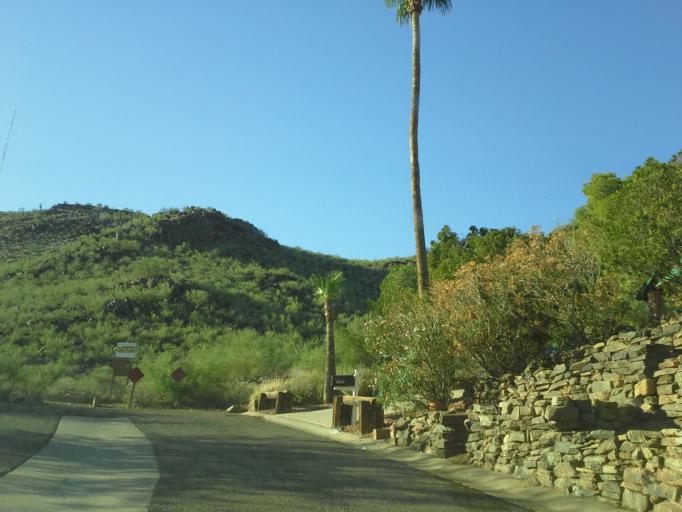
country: US
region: Arizona
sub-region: Maricopa County
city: Glendale
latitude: 33.6015
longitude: -112.0952
